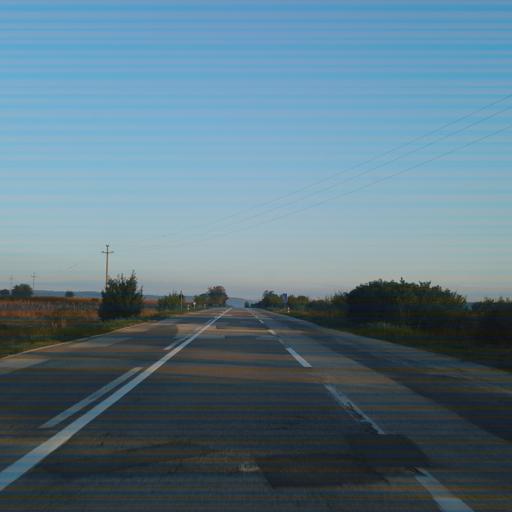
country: RS
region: Central Serbia
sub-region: Zajecarski Okrug
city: Zajecar
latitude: 44.0349
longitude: 22.3412
